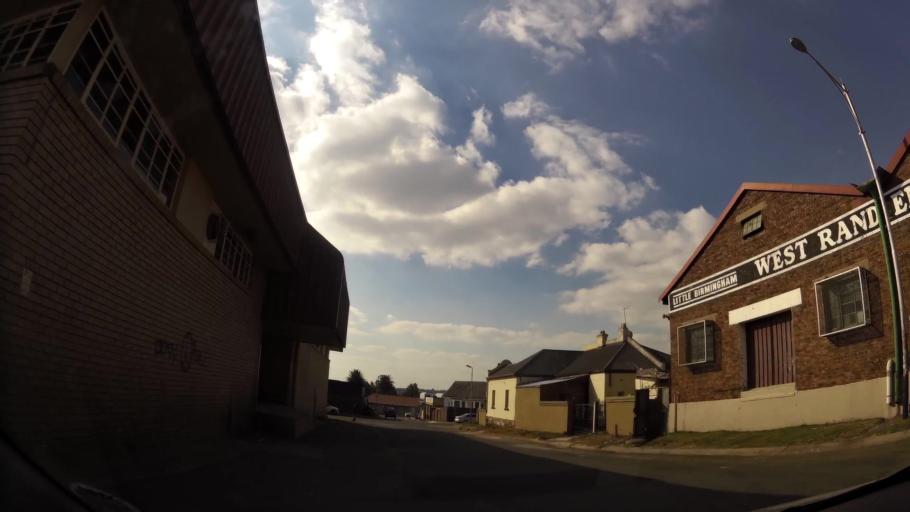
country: ZA
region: Gauteng
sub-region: West Rand District Municipality
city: Krugersdorp
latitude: -26.1073
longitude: 27.7720
